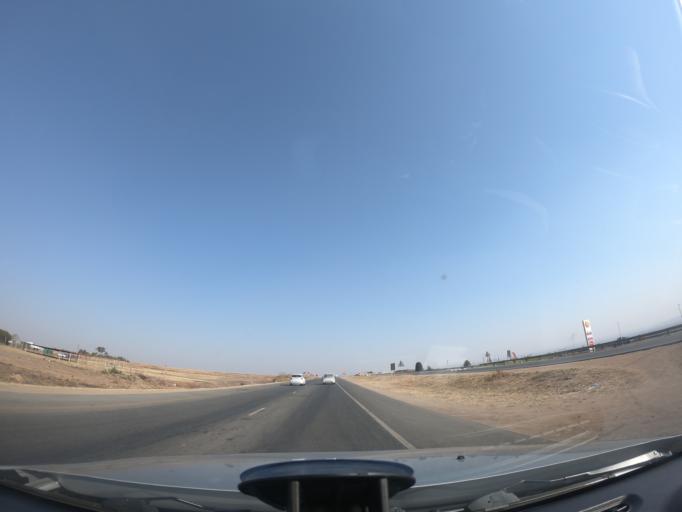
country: ZA
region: Gauteng
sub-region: City of Johannesburg Metropolitan Municipality
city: Diepsloot
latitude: -25.9070
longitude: 28.0271
